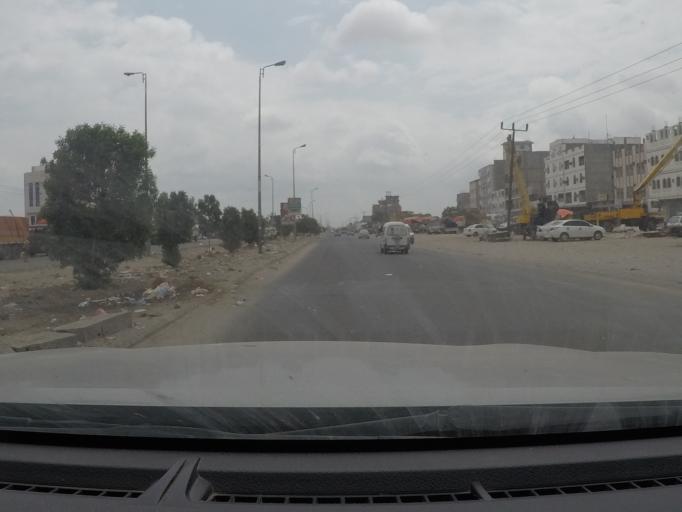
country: YE
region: Lahij
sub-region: Al  Hawtah
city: Lahij
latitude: 12.9905
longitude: 44.9338
